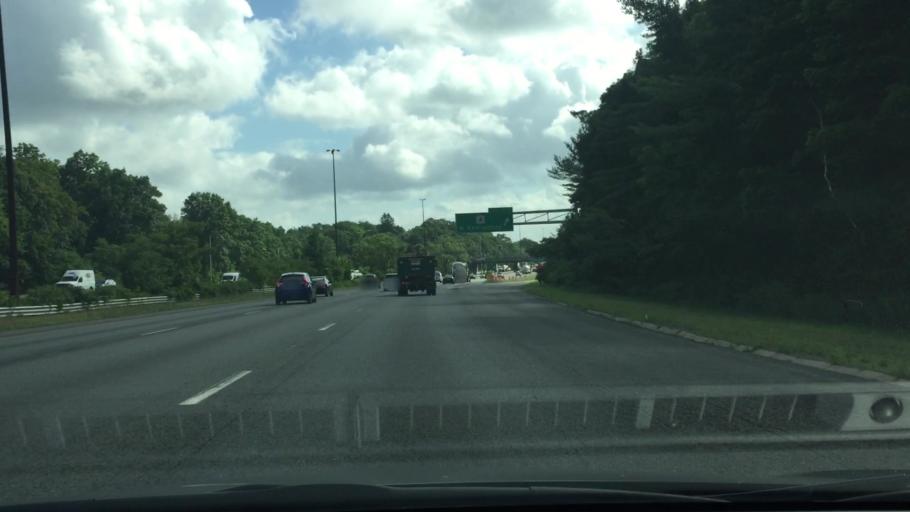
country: US
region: Massachusetts
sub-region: Middlesex County
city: Chelmsford
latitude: 42.6013
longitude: -71.3591
